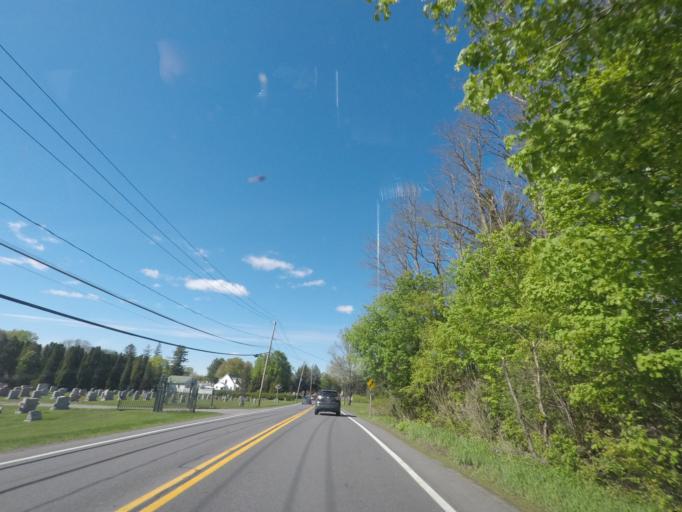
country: US
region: New York
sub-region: Albany County
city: Delmar
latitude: 42.5963
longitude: -73.7954
